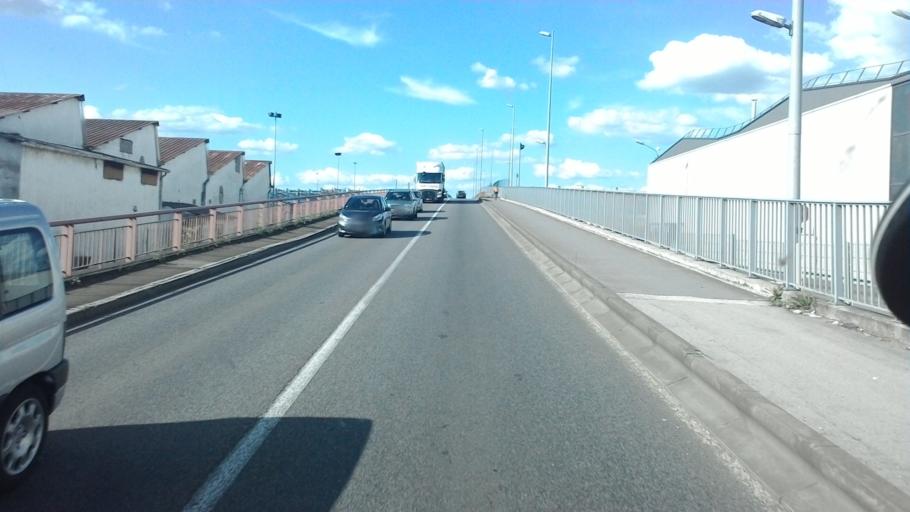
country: FR
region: Franche-Comte
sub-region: Departement de la Haute-Saone
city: Noidans-les-Vesoul
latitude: 47.6185
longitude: 6.1349
